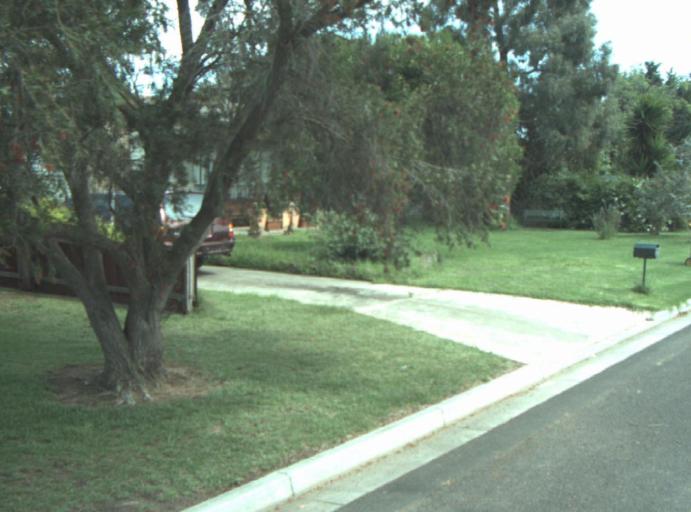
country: AU
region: Victoria
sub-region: Wyndham
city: Little River
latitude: -37.9698
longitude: 144.5065
